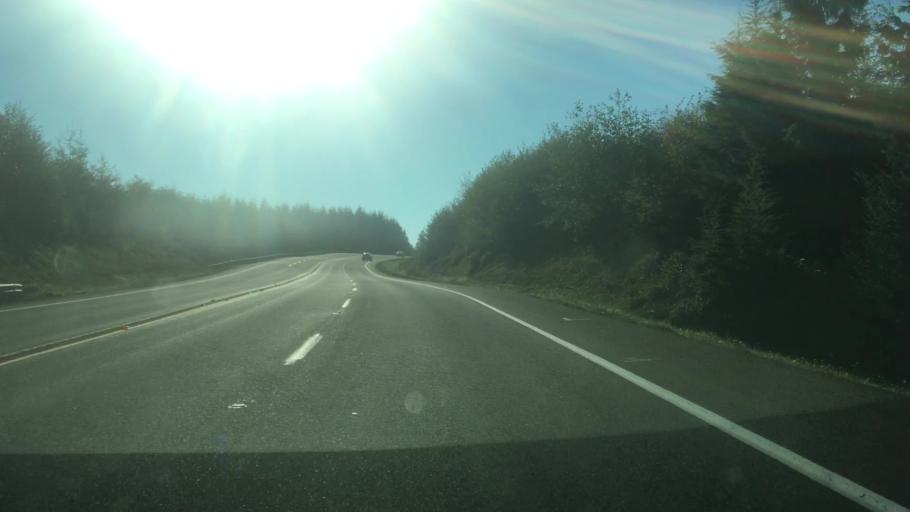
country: US
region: Washington
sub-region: Pacific County
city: South Bend
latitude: 46.6848
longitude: -123.8870
